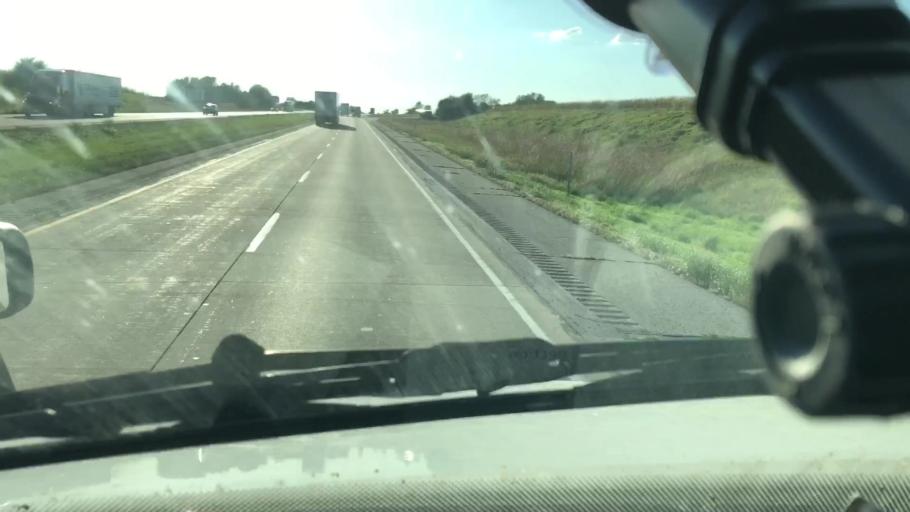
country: US
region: Iowa
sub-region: Pottawattamie County
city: Avoca
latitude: 41.4992
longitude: -95.4861
